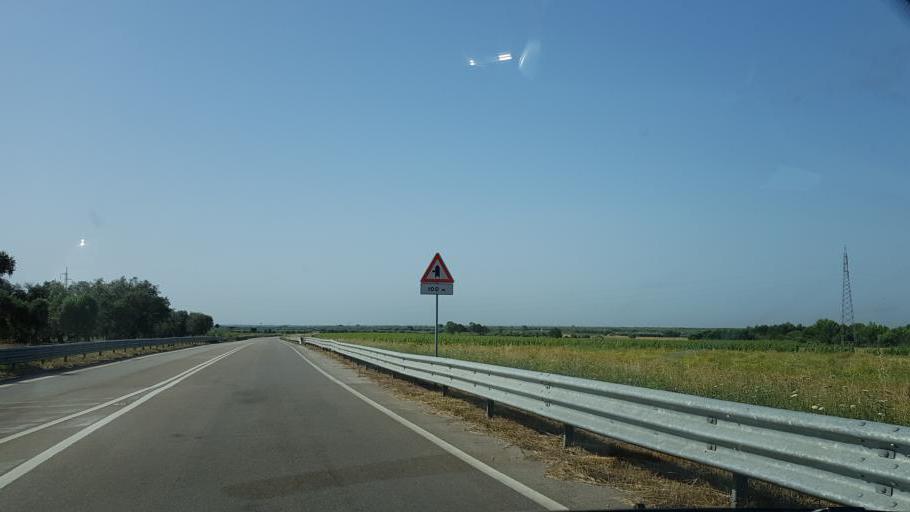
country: IT
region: Apulia
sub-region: Provincia di Brindisi
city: San Pancrazio Salentino
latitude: 40.4852
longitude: 17.8342
